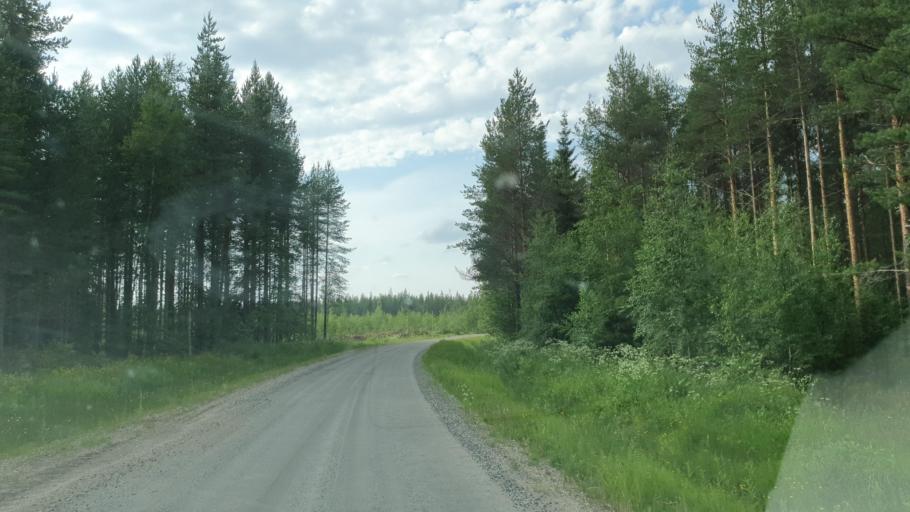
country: FI
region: Kainuu
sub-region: Kehys-Kainuu
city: Kuhmo
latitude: 64.0645
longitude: 29.7498
